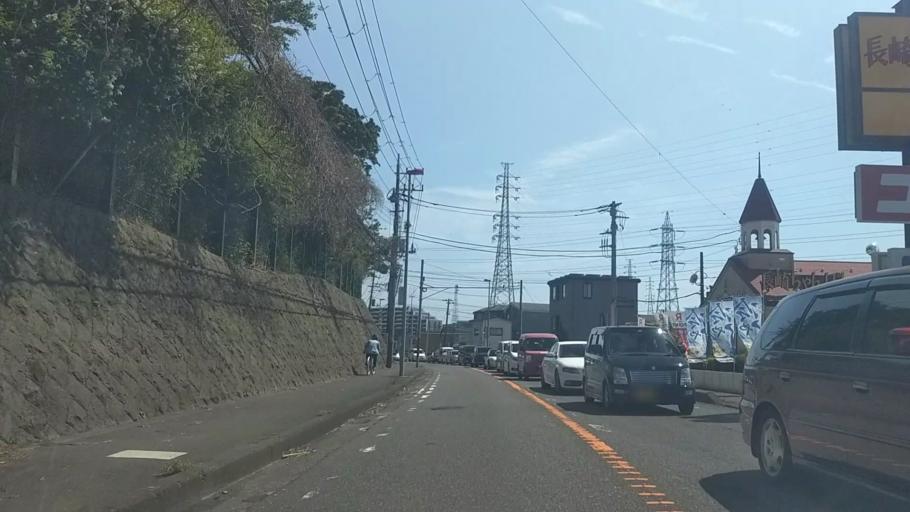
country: JP
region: Kanagawa
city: Kamakura
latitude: 35.3577
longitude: 139.5457
